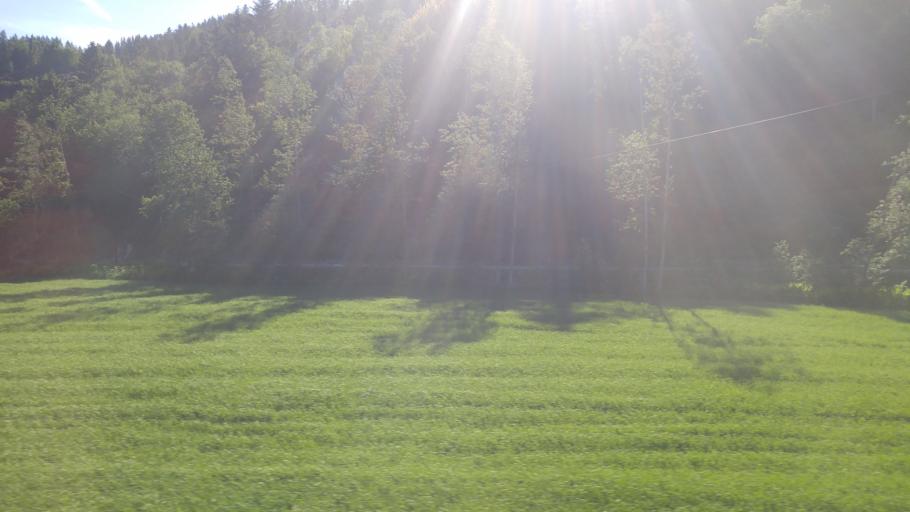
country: NO
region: Sor-Trondelag
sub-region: Midtre Gauldal
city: Storen
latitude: 63.0940
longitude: 10.2357
